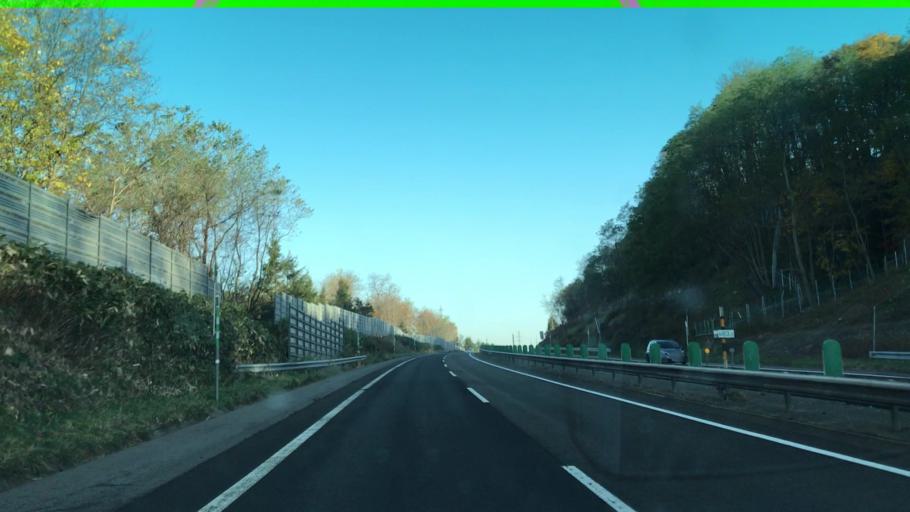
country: JP
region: Hokkaido
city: Sunagawa
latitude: 43.4198
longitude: 141.9110
